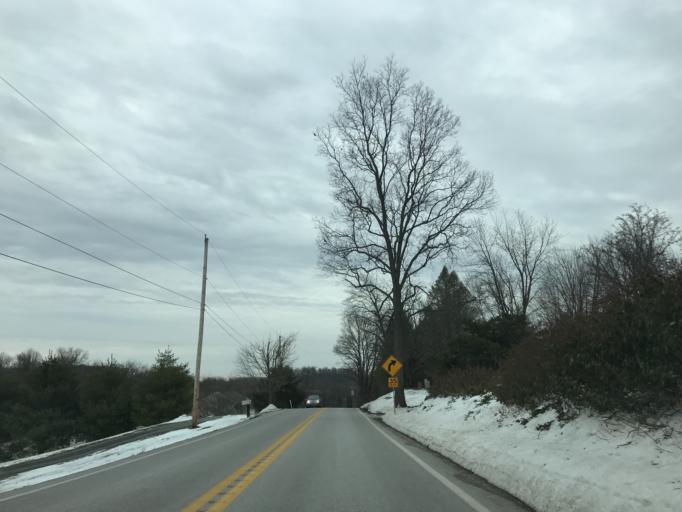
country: US
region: Pennsylvania
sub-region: York County
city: New Freedom
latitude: 39.7263
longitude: -76.7246
